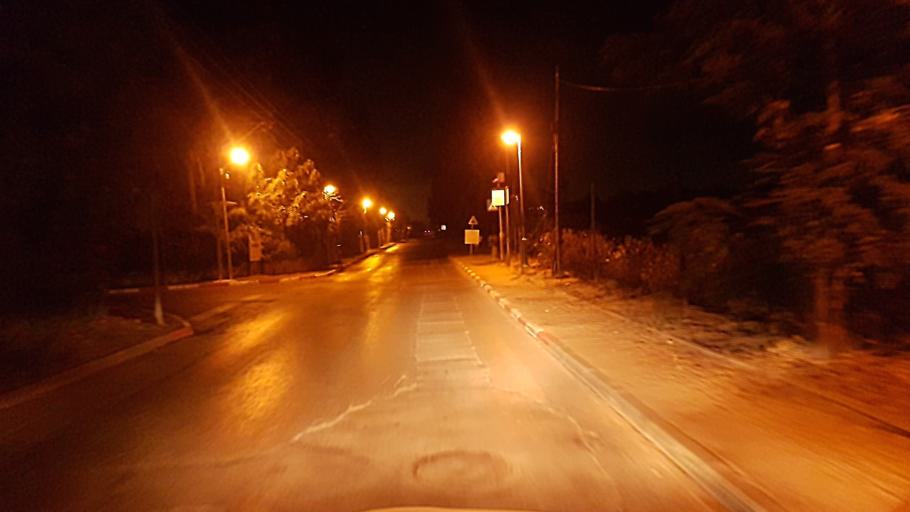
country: IL
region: Central District
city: Hod HaSharon
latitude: 32.1642
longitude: 34.8762
